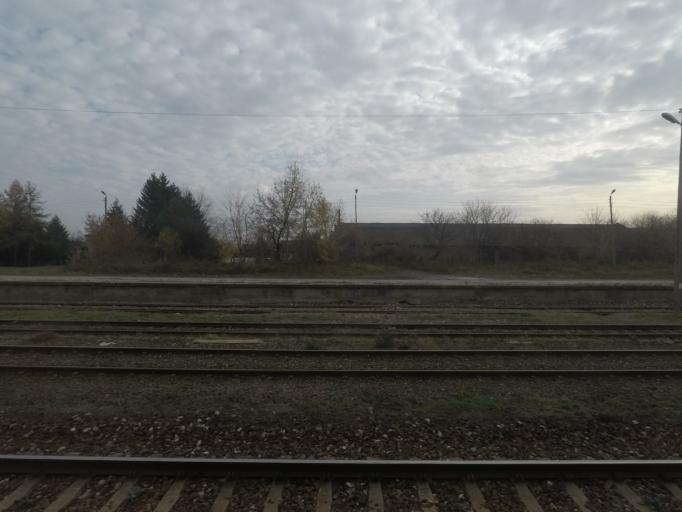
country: PL
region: Subcarpathian Voivodeship
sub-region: Powiat przemyski
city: Zurawica
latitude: 49.8206
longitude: 22.8260
